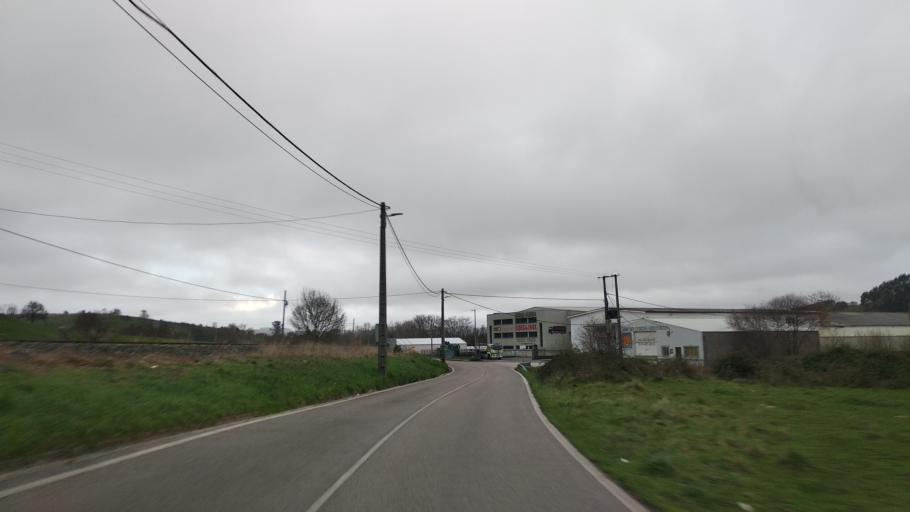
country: ES
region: Cantabria
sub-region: Provincia de Cantabria
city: Entrambasaguas
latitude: 43.3985
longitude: -3.7313
